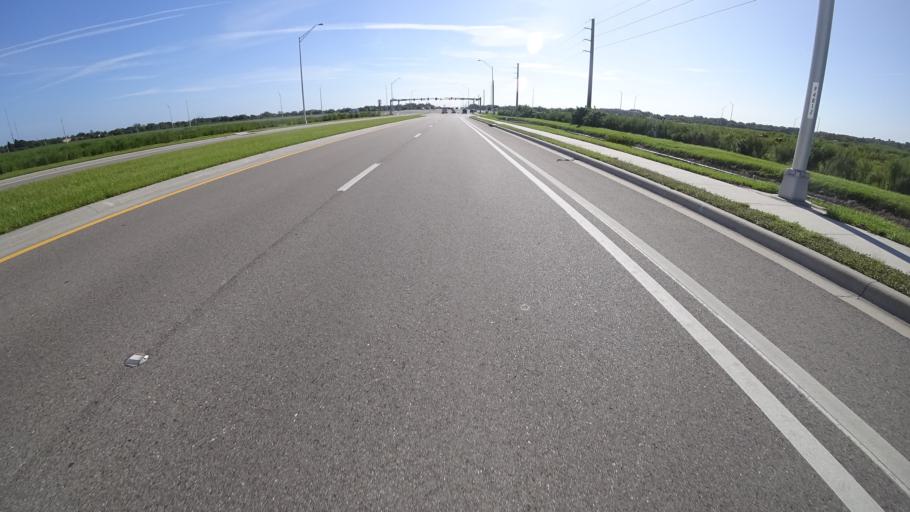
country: US
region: Florida
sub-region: Manatee County
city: Samoset
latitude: 27.4617
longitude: -82.5325
